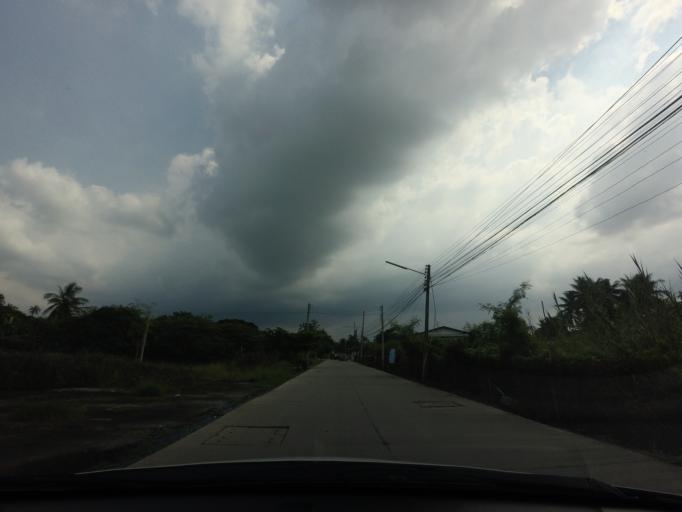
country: TH
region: Nakhon Pathom
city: Nakhon Chai Si
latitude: 13.7857
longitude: 100.2330
